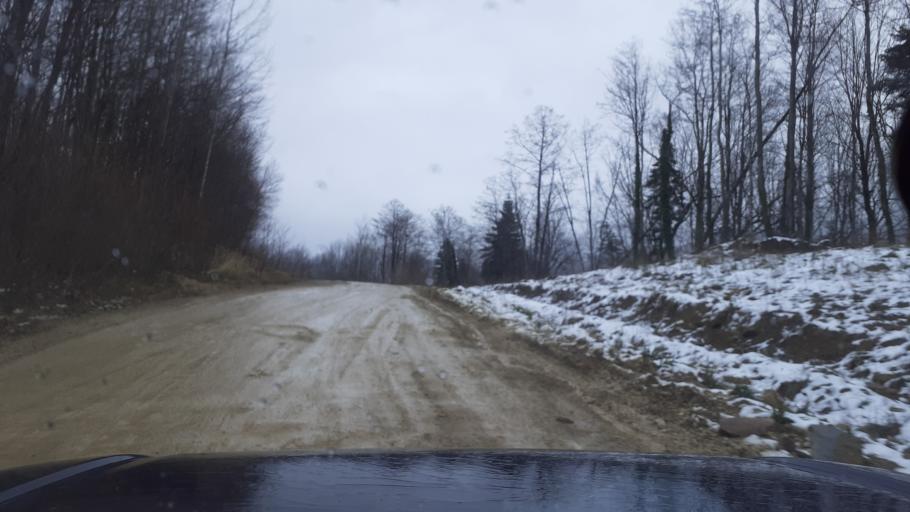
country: RU
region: Krasnodarskiy
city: Neftegorsk
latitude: 44.1325
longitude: 39.8124
